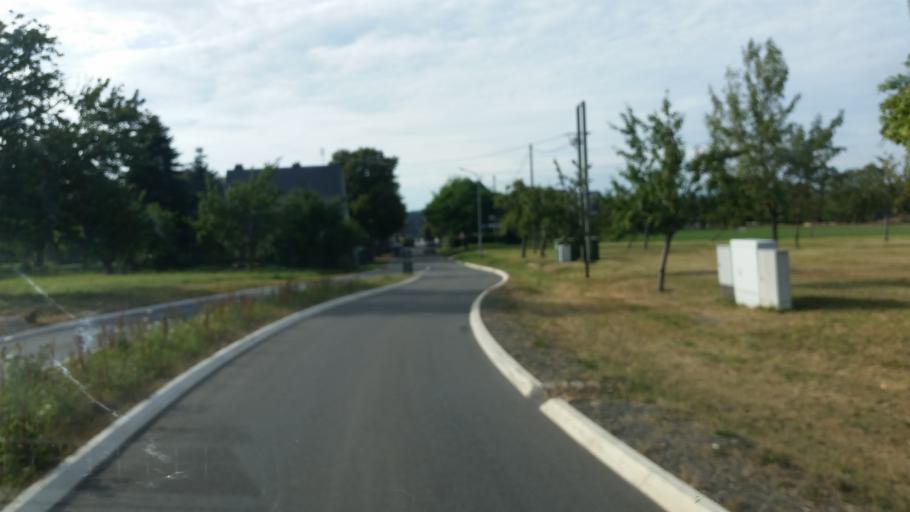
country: DE
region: Rheinland-Pfalz
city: Raversbeuren
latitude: 49.9539
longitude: 7.2303
